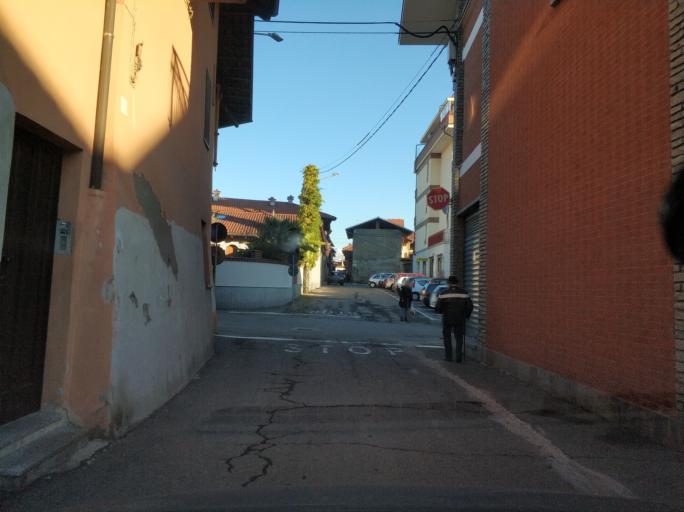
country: IT
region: Piedmont
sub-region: Provincia di Torino
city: Nole
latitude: 45.2433
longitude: 7.5709
